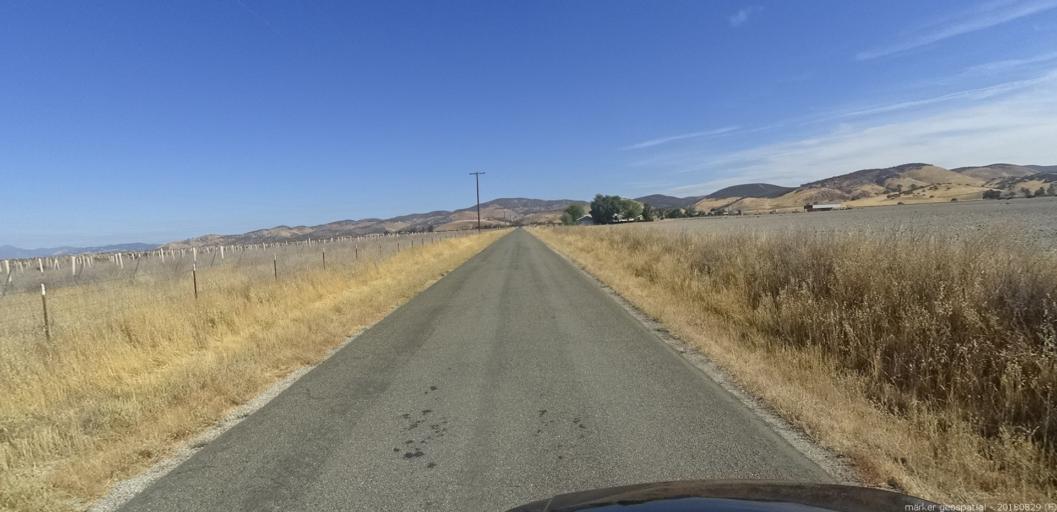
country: US
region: California
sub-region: Monterey County
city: King City
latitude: 35.9520
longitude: -121.0820
